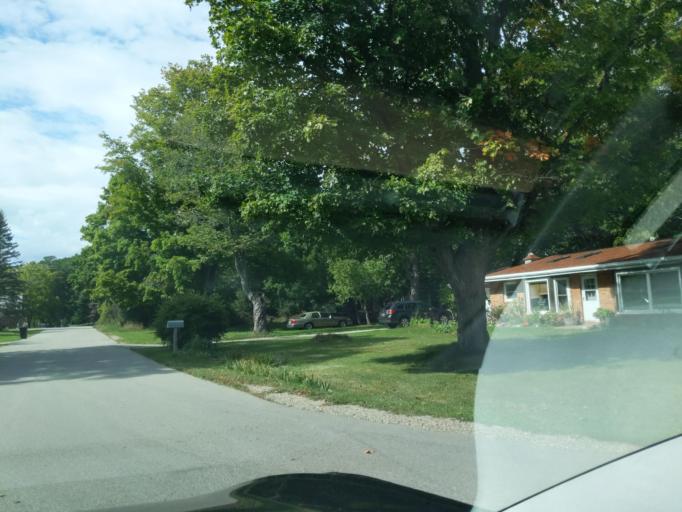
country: US
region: Michigan
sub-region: Antrim County
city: Bellaire
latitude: 45.0761
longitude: -85.3561
